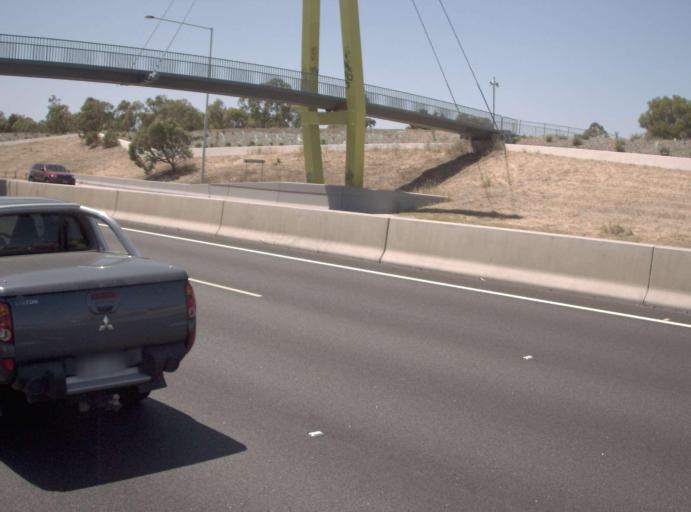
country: AU
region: Victoria
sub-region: Brimbank
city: Albion
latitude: -37.7544
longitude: 144.8267
